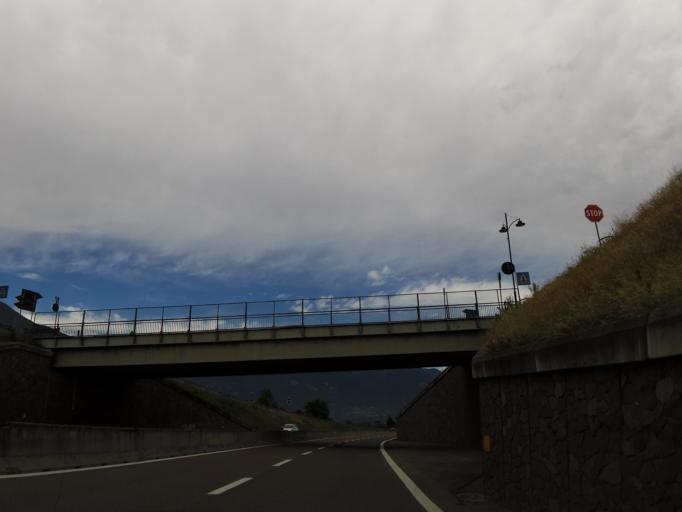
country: IT
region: Trentino-Alto Adige
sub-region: Bolzano
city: Postal
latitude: 46.6091
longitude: 11.1800
